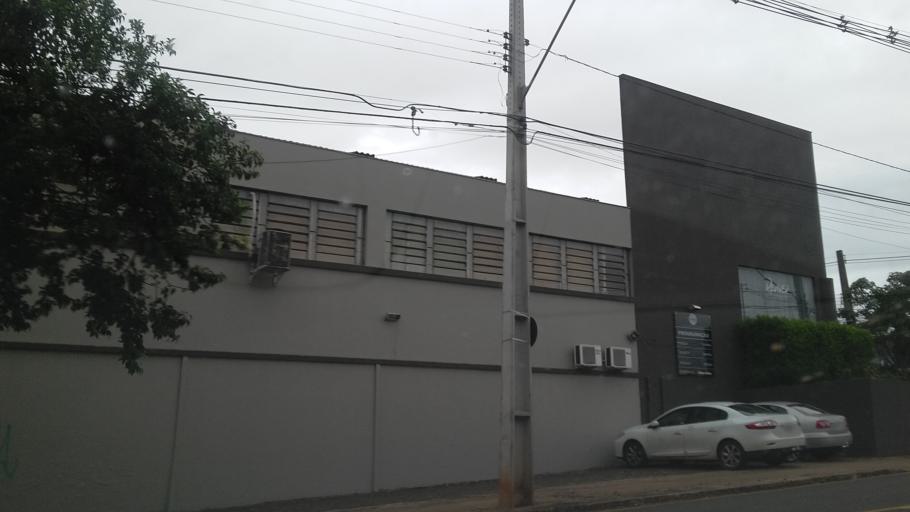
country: BR
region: Parana
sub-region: Londrina
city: Londrina
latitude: -23.3216
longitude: -51.1770
